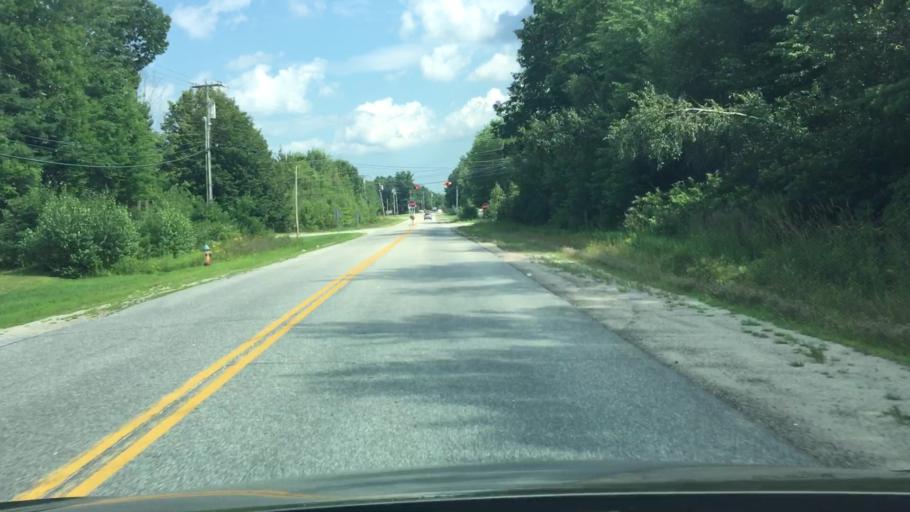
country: US
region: Maine
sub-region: Androscoggin County
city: Auburn
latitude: 44.0786
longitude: -70.2610
